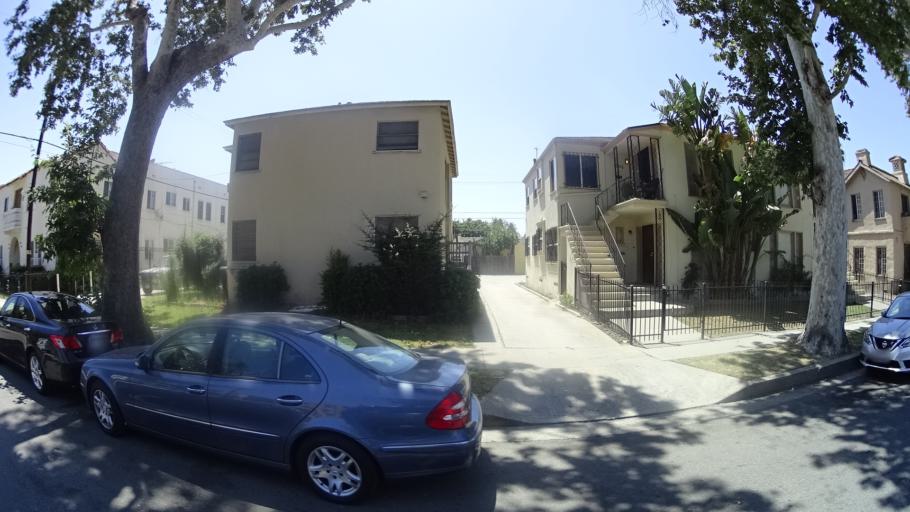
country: US
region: California
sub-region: Los Angeles County
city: View Park-Windsor Hills
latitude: 34.0057
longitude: -118.3259
